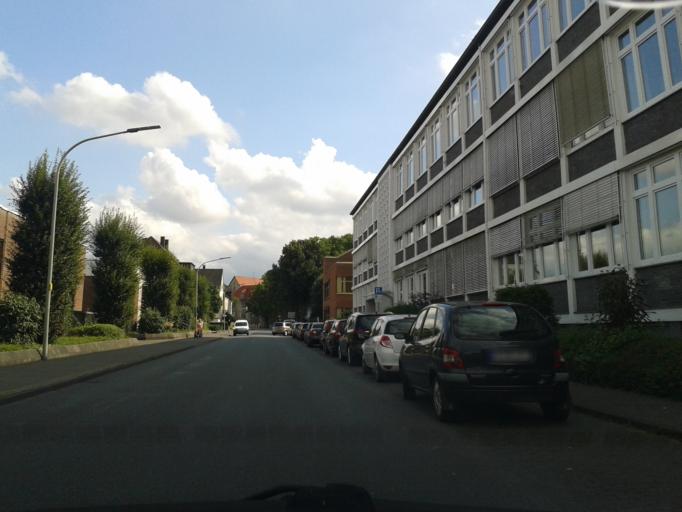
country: DE
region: North Rhine-Westphalia
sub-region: Regierungsbezirk Detmold
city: Paderborn
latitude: 51.7251
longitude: 8.7549
